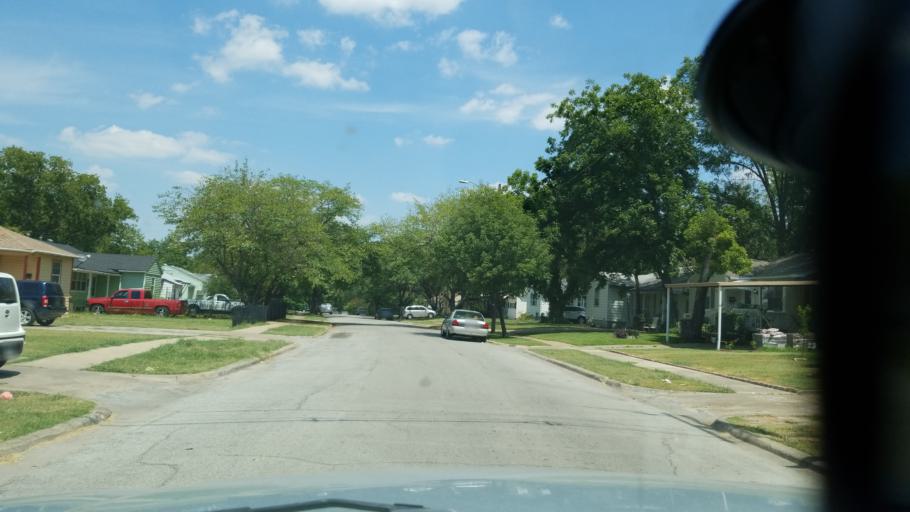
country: US
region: Texas
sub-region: Dallas County
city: Grand Prairie
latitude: 32.7560
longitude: -96.9767
